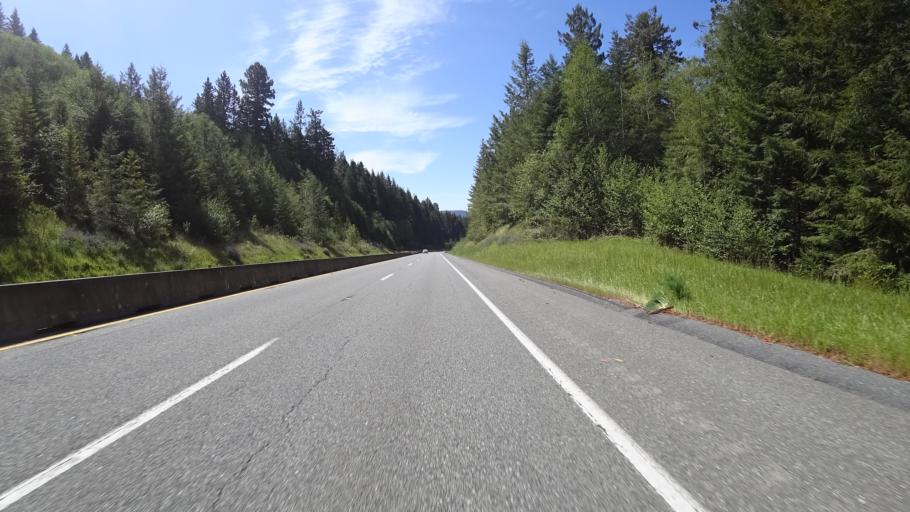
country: US
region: California
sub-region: Humboldt County
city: Westhaven-Moonstone
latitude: 41.3626
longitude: -123.9897
